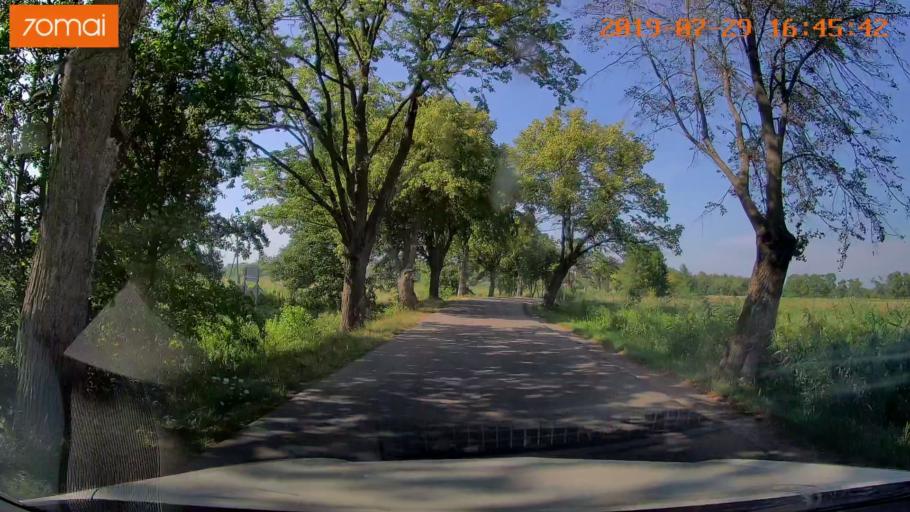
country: RU
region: Kaliningrad
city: Primorsk
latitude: 54.7672
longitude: 20.0795
